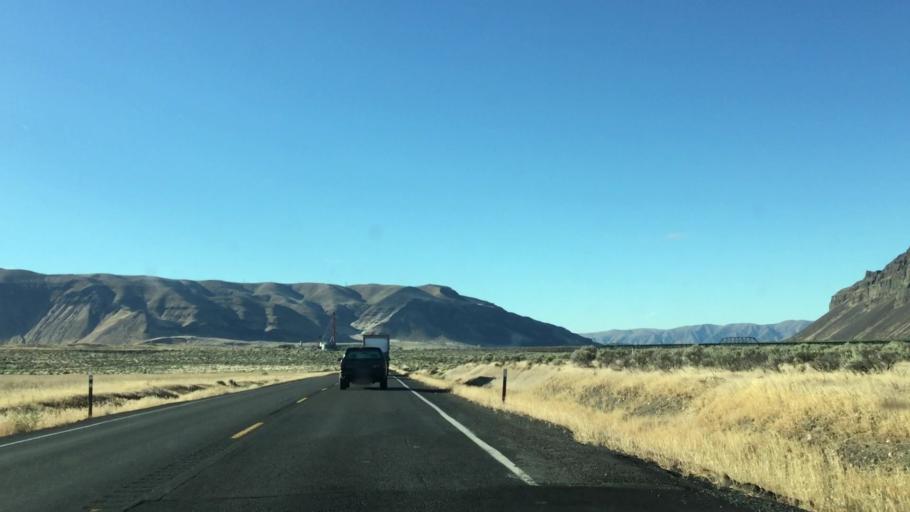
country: US
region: Washington
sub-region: Grant County
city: Mattawa
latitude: 46.8513
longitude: -119.9437
